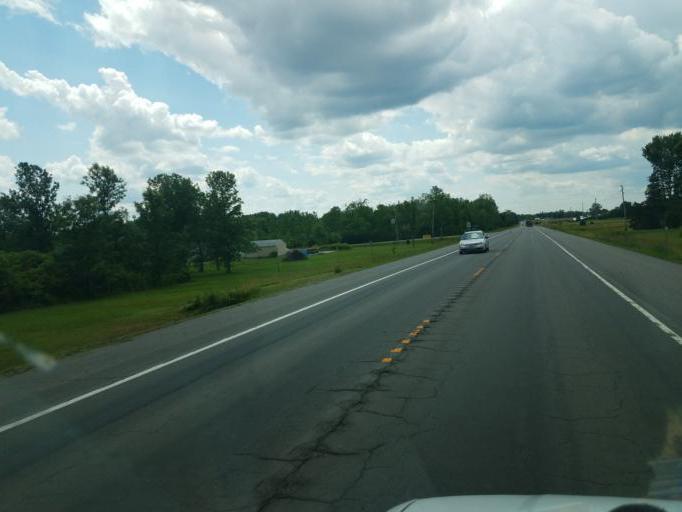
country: US
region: New York
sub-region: Seneca County
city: Waterloo
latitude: 42.9604
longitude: -76.8596
